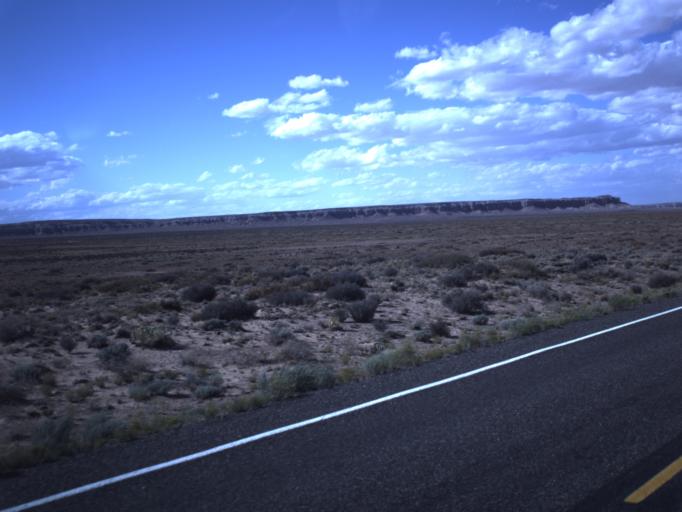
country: US
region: Utah
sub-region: Wayne County
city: Loa
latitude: 38.1724
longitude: -110.6243
